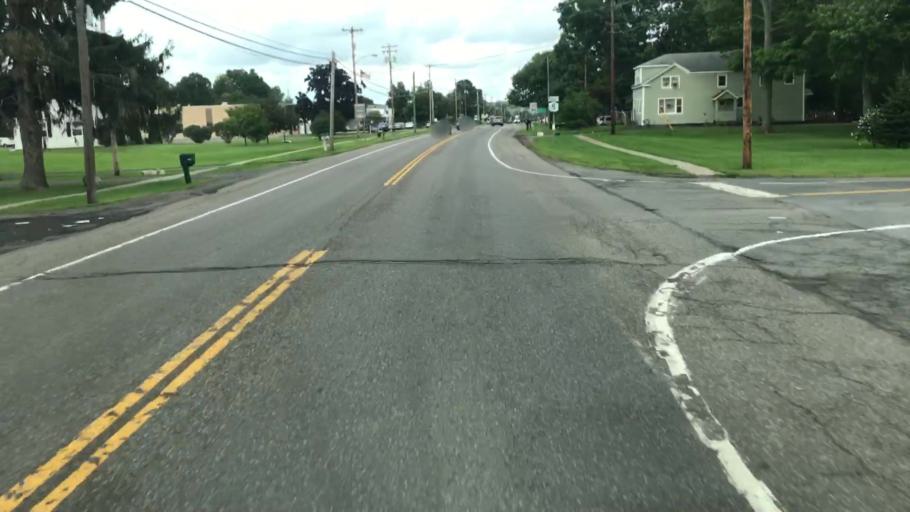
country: US
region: New York
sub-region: Onondaga County
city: Elbridge
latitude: 43.0371
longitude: -76.4330
